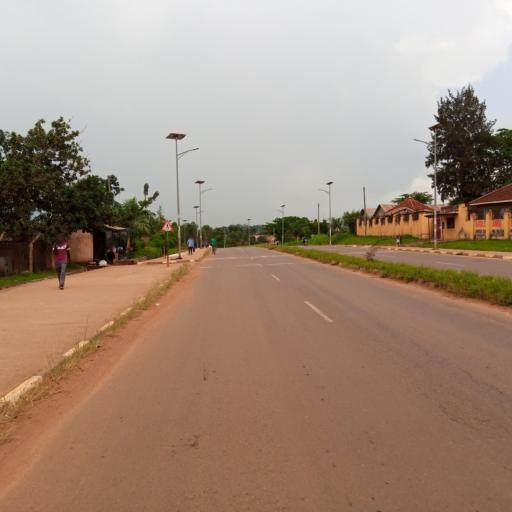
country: UG
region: Eastern Region
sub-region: Mbale District
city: Mbale
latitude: 1.0823
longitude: 34.1763
